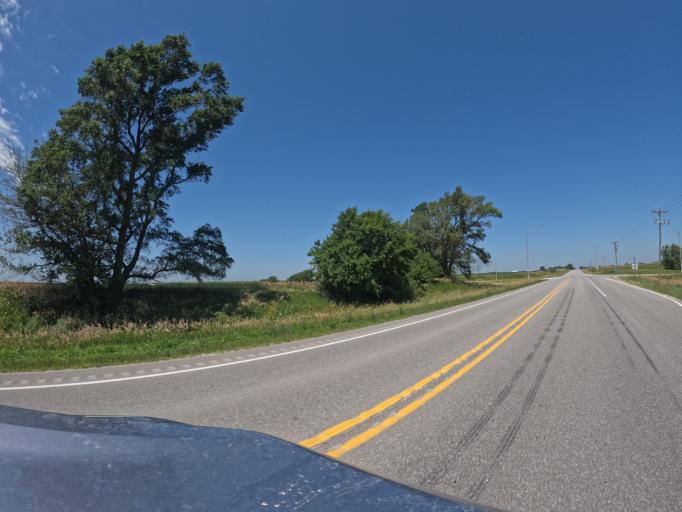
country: US
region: Iowa
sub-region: Keokuk County
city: Sigourney
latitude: 41.4513
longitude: -92.3550
